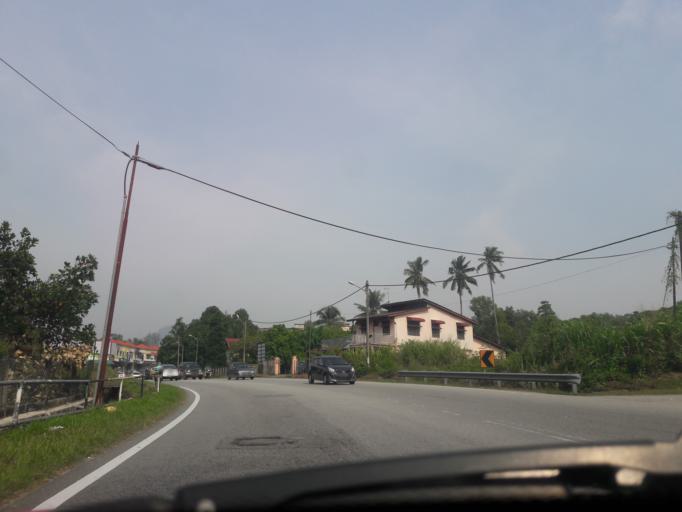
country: MY
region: Kedah
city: Kulim
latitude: 5.3671
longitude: 100.5489
